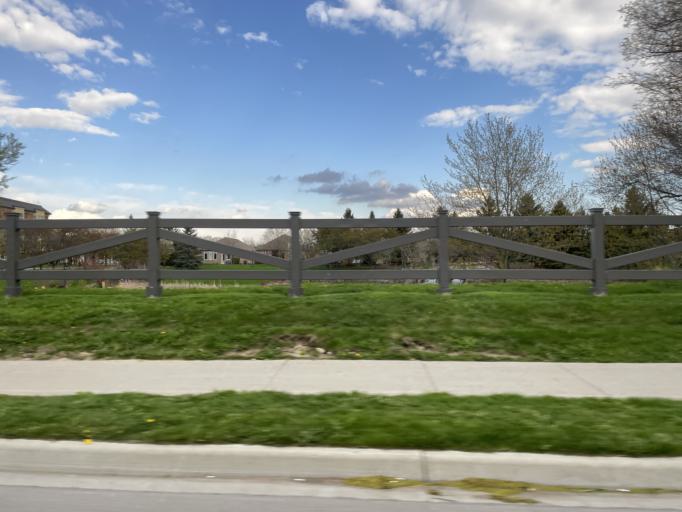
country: CA
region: Ontario
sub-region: Wellington County
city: Guelph
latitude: 43.5314
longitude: -80.2181
